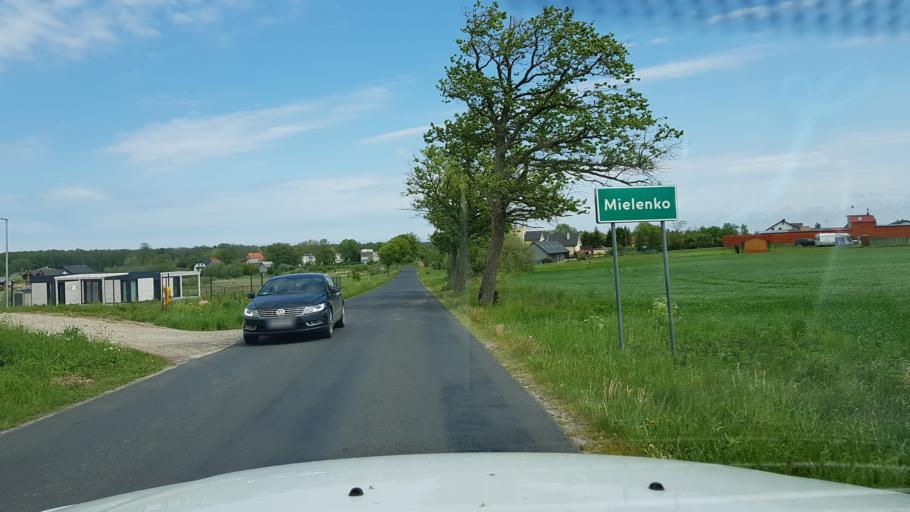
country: PL
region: West Pomeranian Voivodeship
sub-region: Powiat koszalinski
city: Mielno
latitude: 54.2456
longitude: 16.0057
